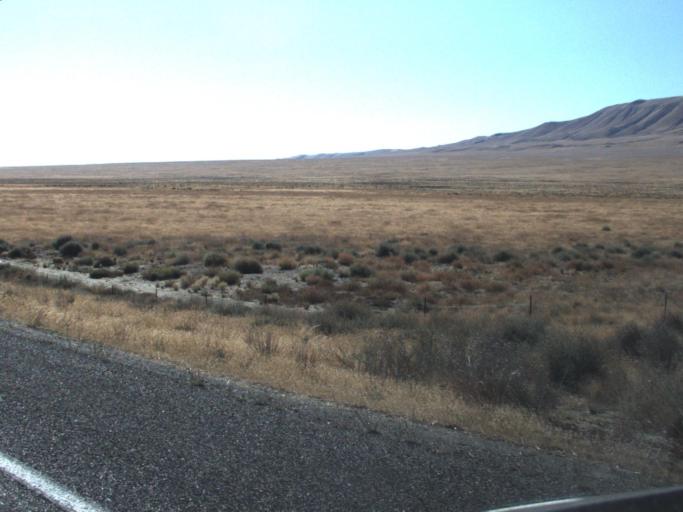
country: US
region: Washington
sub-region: Benton County
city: Benton City
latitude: 46.4910
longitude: -119.5923
